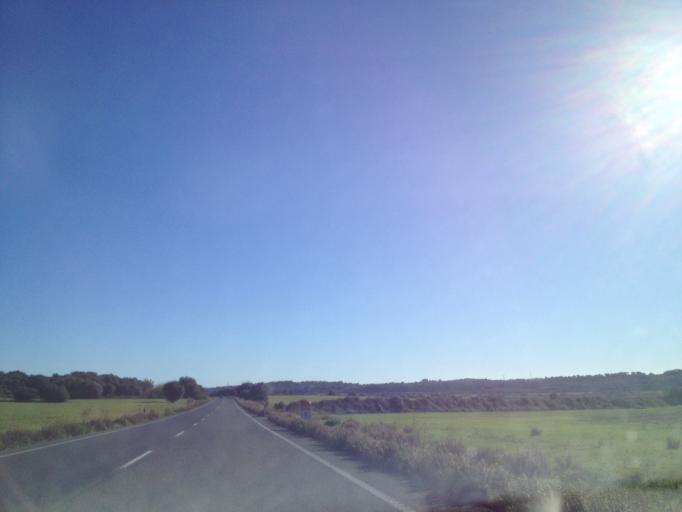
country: ES
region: Balearic Islands
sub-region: Illes Balears
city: Maria de la Salut
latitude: 39.6437
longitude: 3.0458
